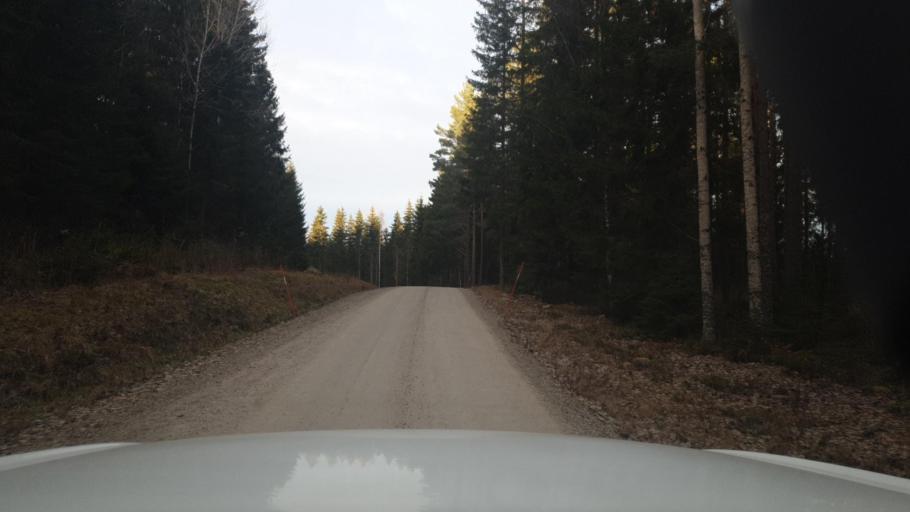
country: SE
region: Vaermland
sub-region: Arvika Kommun
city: Arvika
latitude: 59.5827
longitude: 12.8190
